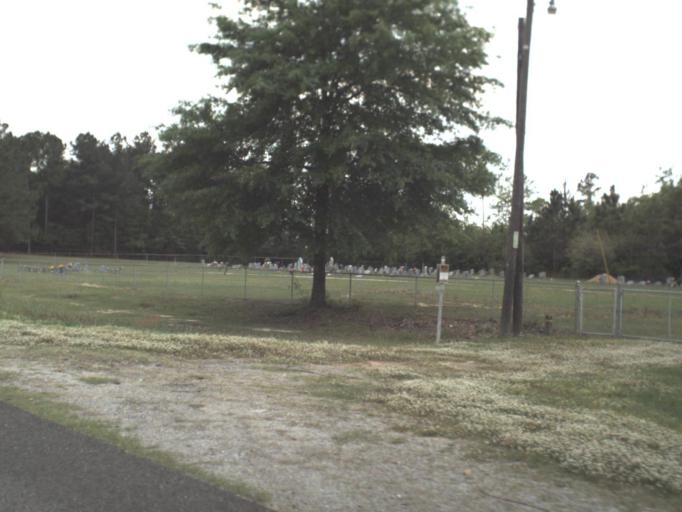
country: US
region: Florida
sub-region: Escambia County
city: Cantonment
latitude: 30.6503
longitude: -87.3514
